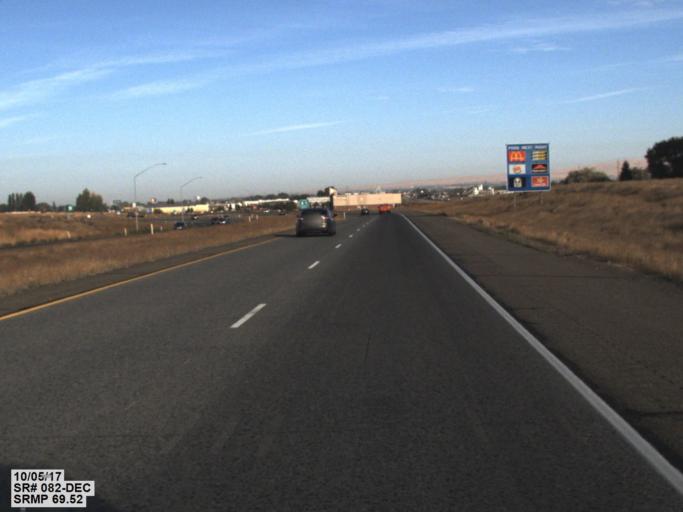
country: US
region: Washington
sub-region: Yakima County
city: Sunnyside
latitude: 46.3035
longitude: -119.9677
